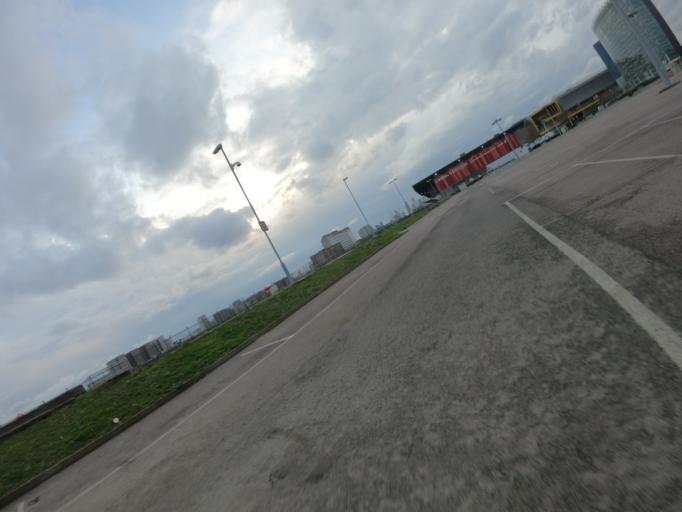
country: GB
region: England
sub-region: Greater London
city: East Ham
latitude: 51.5075
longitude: 0.0376
